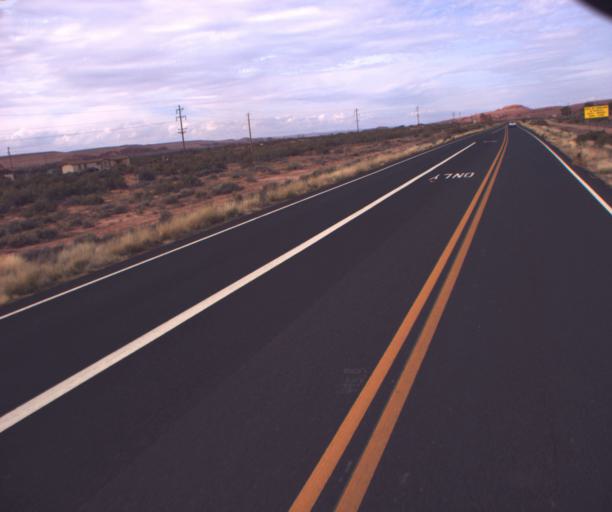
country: US
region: Arizona
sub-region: Apache County
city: Many Farms
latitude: 36.7271
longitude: -109.6304
